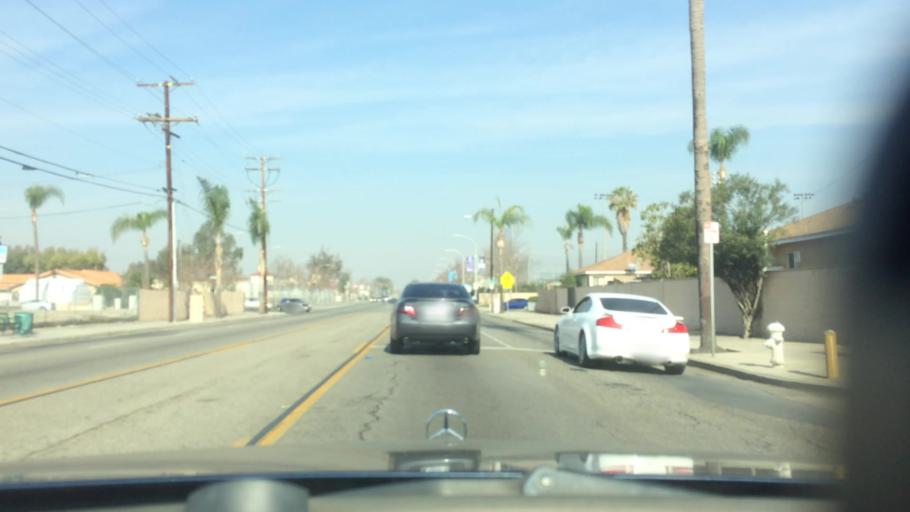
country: US
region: California
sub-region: Orange County
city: Santa Ana
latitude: 33.7224
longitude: -117.8852
